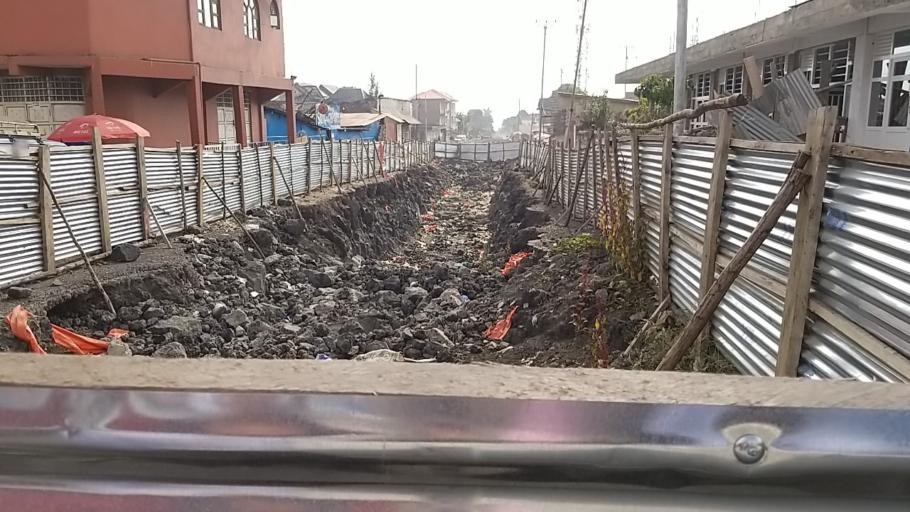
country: CD
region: Nord Kivu
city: Goma
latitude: -1.6845
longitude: 29.2350
